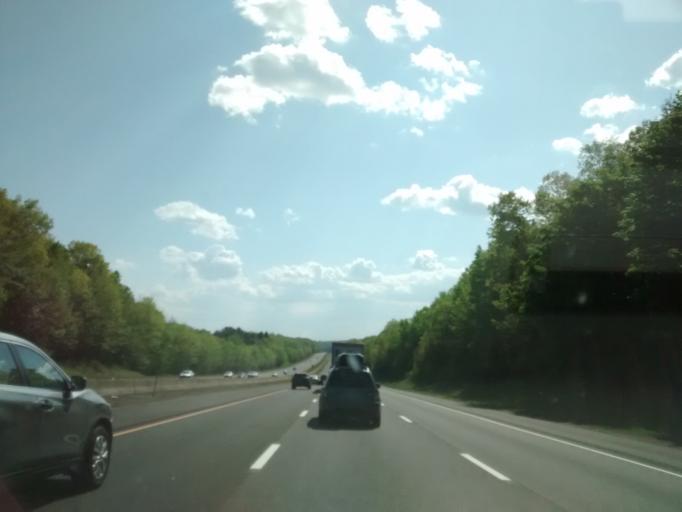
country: US
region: Connecticut
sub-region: Tolland County
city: Stafford Springs
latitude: 41.9359
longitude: -72.2354
